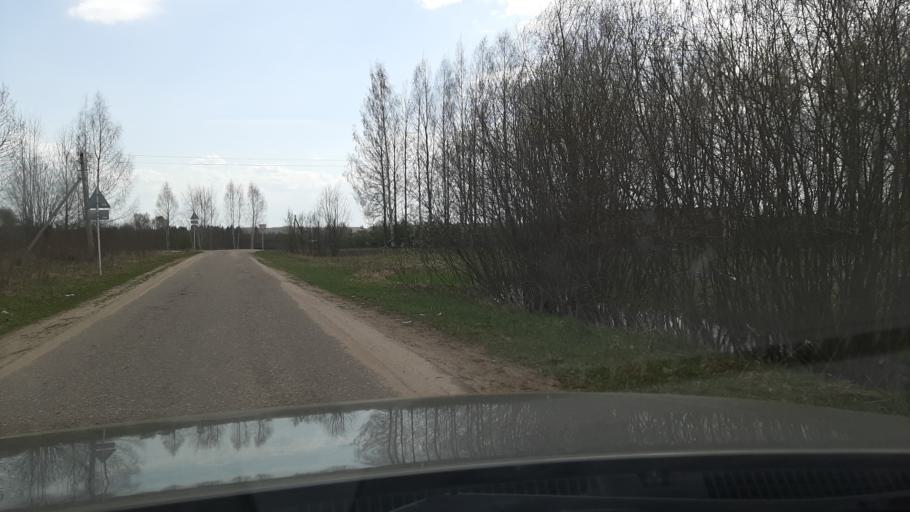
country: RU
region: Ivanovo
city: Furmanov
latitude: 57.3002
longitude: 41.1663
